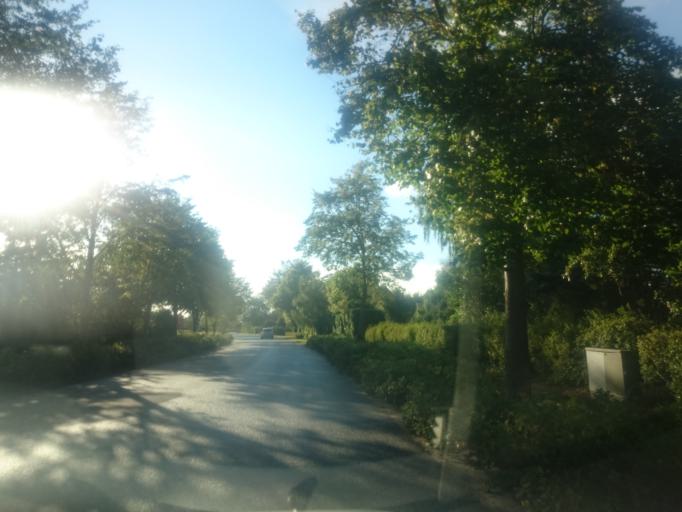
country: DK
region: South Denmark
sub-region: Billund Kommune
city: Billund
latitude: 55.7297
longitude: 9.1082
